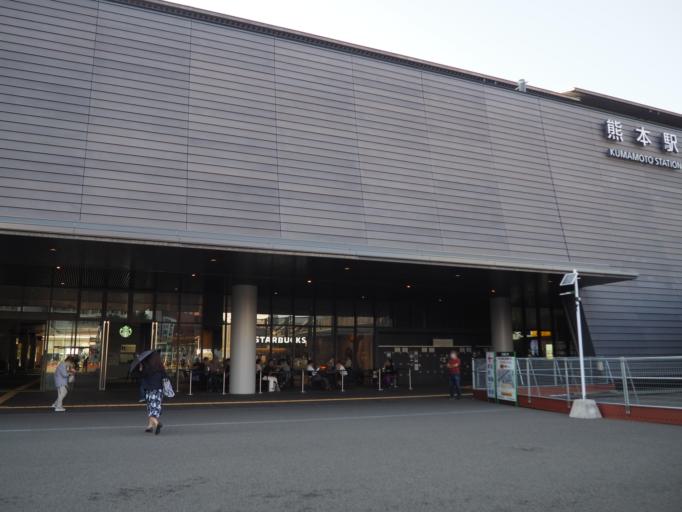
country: JP
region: Kumamoto
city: Kumamoto
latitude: 32.7893
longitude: 130.6892
